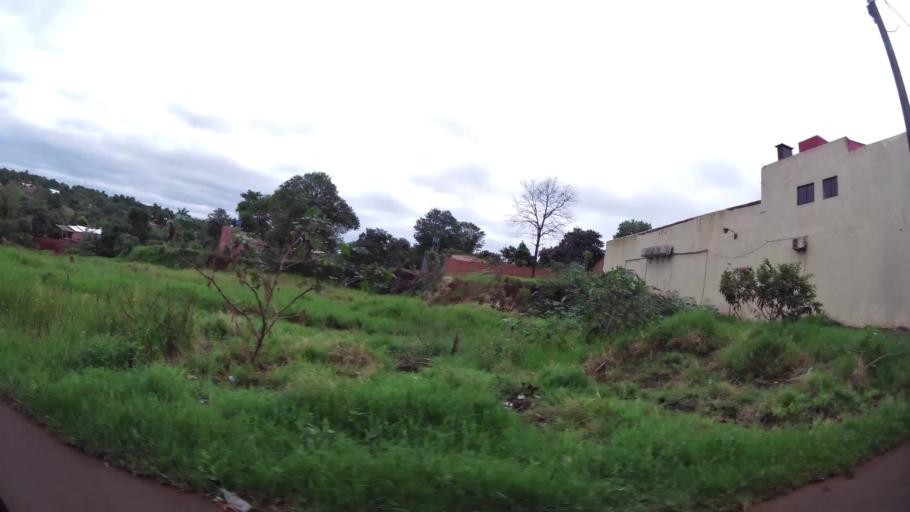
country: PY
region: Alto Parana
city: Ciudad del Este
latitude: -25.4986
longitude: -54.6876
